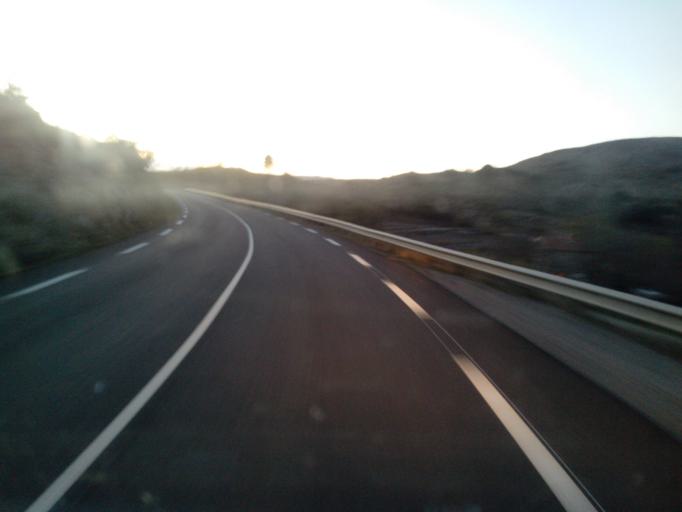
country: FR
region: Languedoc-Roussillon
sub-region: Departement des Pyrenees-Orientales
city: Estagel
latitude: 42.7768
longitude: 2.7259
